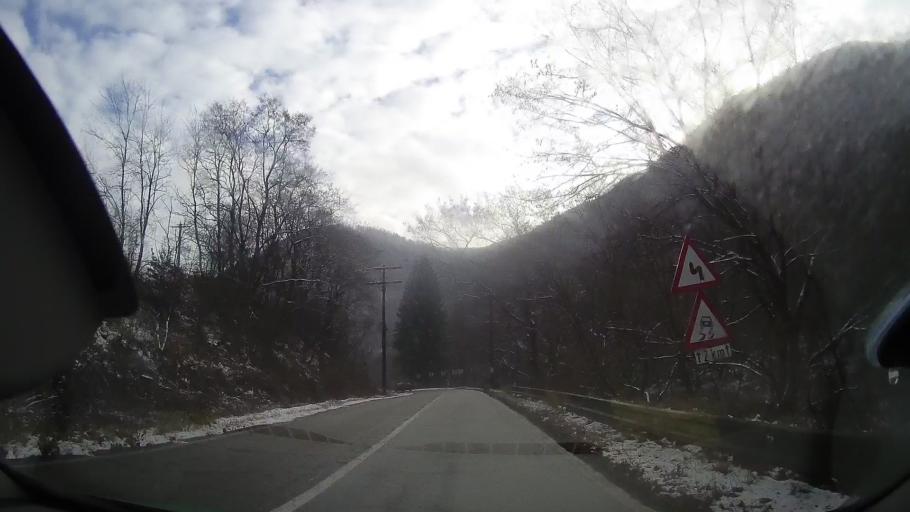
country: RO
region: Alba
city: Salciua de Sus
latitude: 46.3998
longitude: 23.3645
